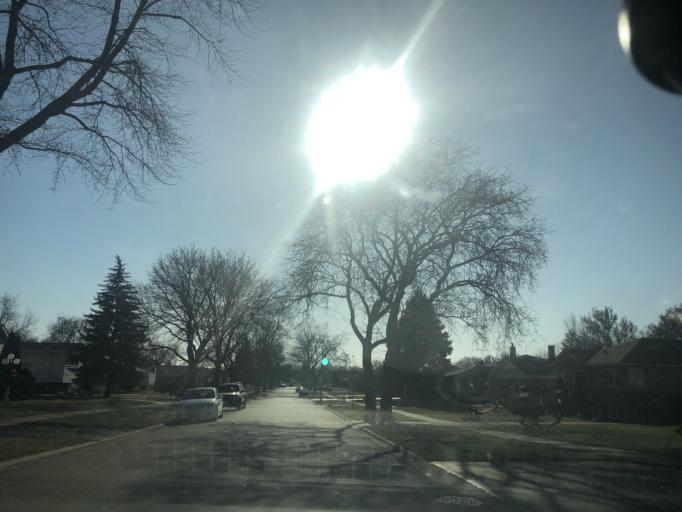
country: US
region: Illinois
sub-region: DuPage County
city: Addison
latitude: 41.9301
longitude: -87.9936
